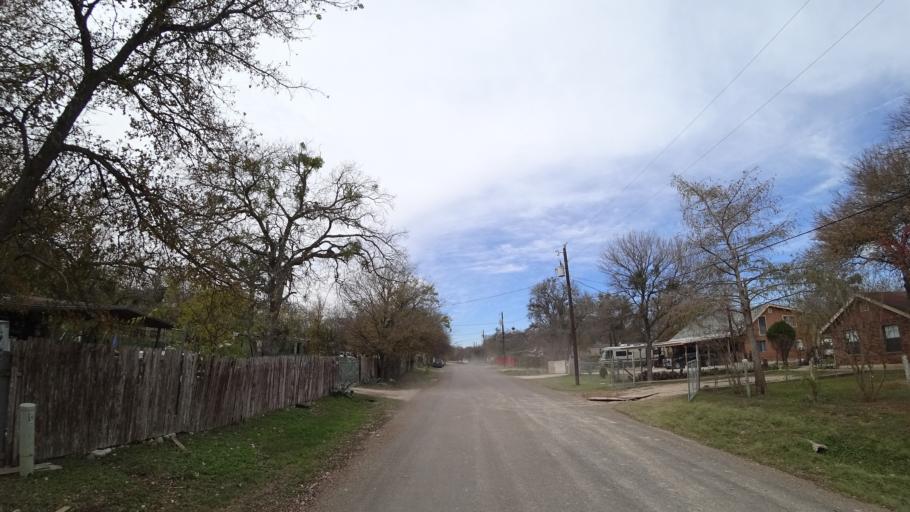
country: US
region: Texas
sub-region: Travis County
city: Garfield
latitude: 30.1341
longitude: -97.5651
